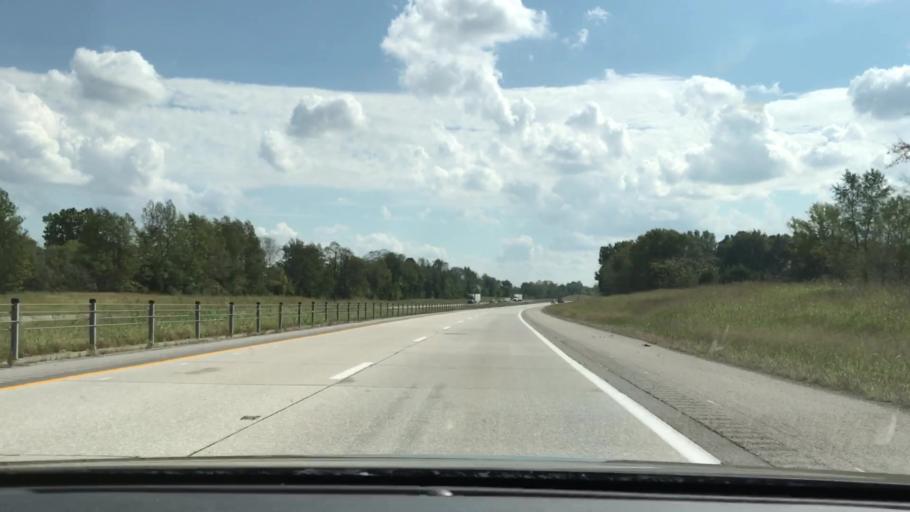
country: US
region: Kentucky
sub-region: Trigg County
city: Cadiz
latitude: 36.8439
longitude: -87.6768
